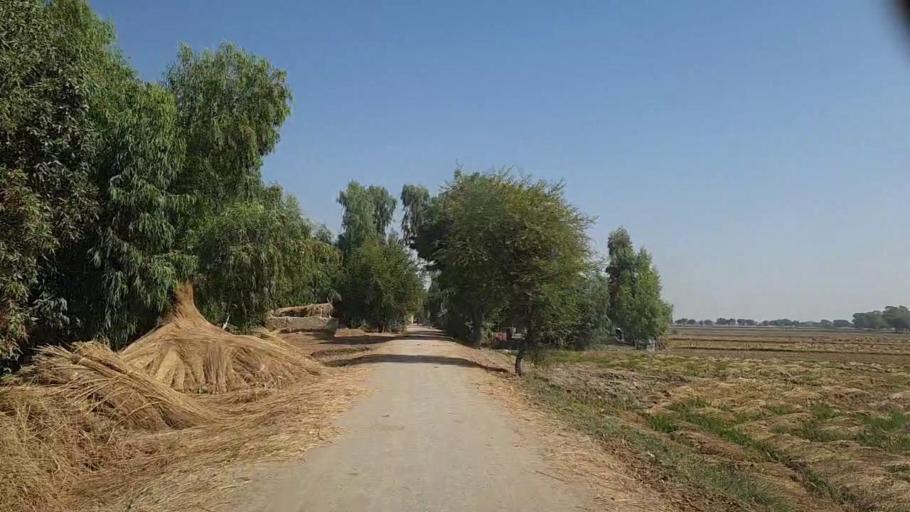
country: PK
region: Sindh
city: Thul
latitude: 28.2561
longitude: 68.8227
